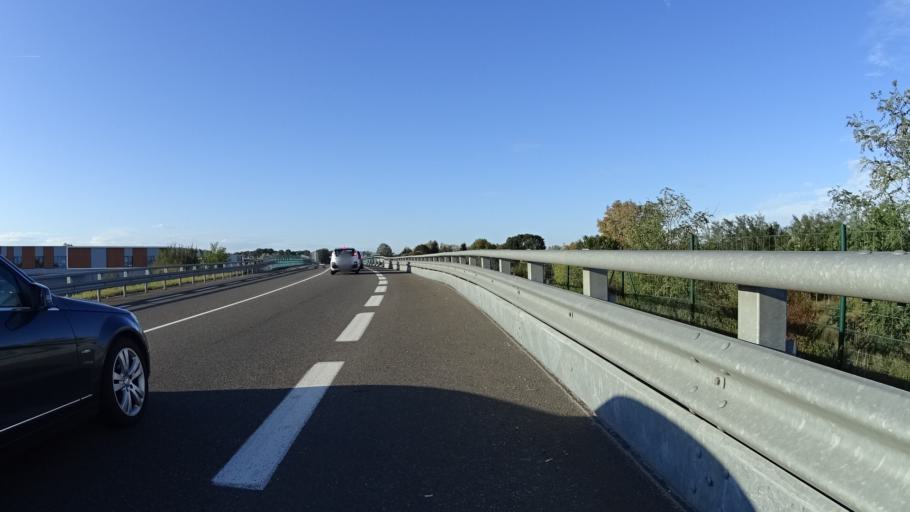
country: FR
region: Aquitaine
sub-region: Departement des Landes
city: Saint-Paul-les-Dax
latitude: 43.7268
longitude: -1.0354
